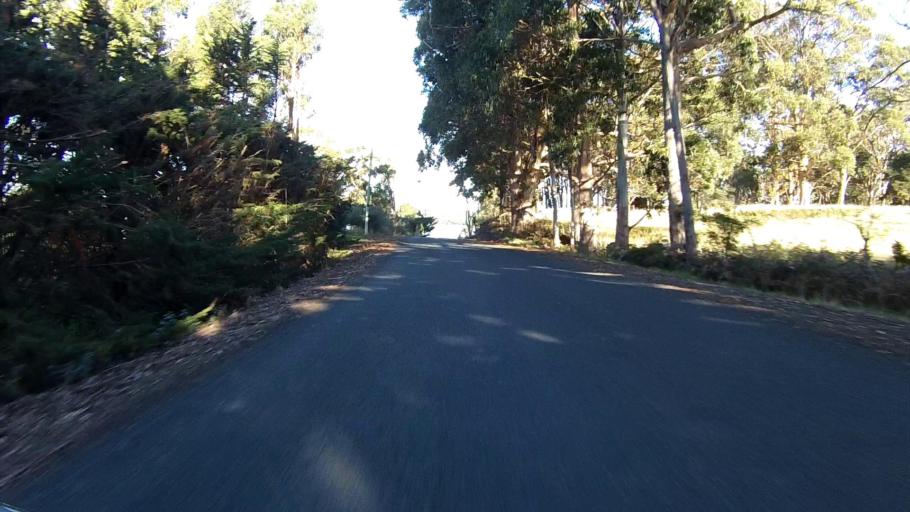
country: AU
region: Tasmania
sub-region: Clarence
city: Sandford
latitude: -43.1719
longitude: 147.8549
